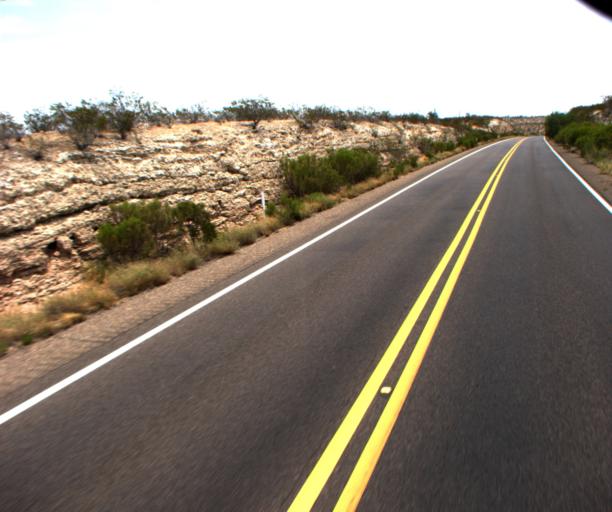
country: US
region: Arizona
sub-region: Gila County
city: Peridot
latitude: 33.2812
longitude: -110.3367
